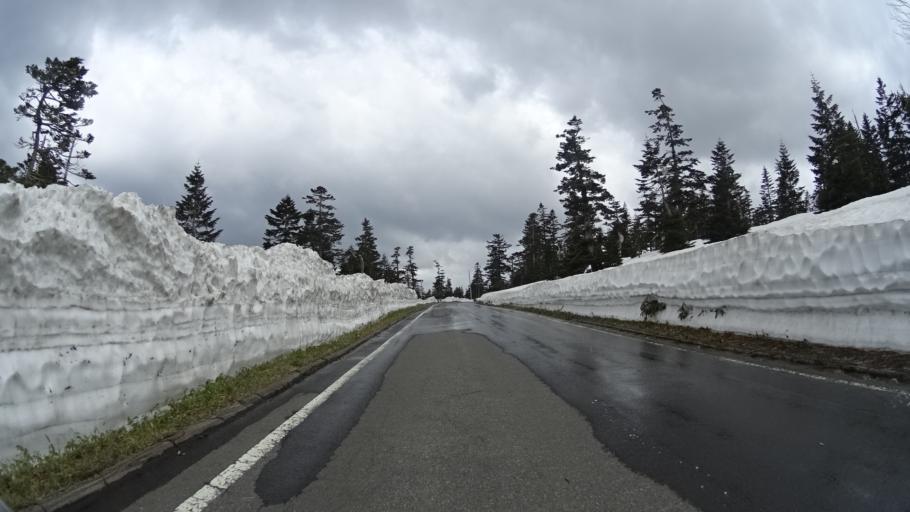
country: JP
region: Nagano
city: Nakano
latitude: 36.6653
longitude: 138.5352
